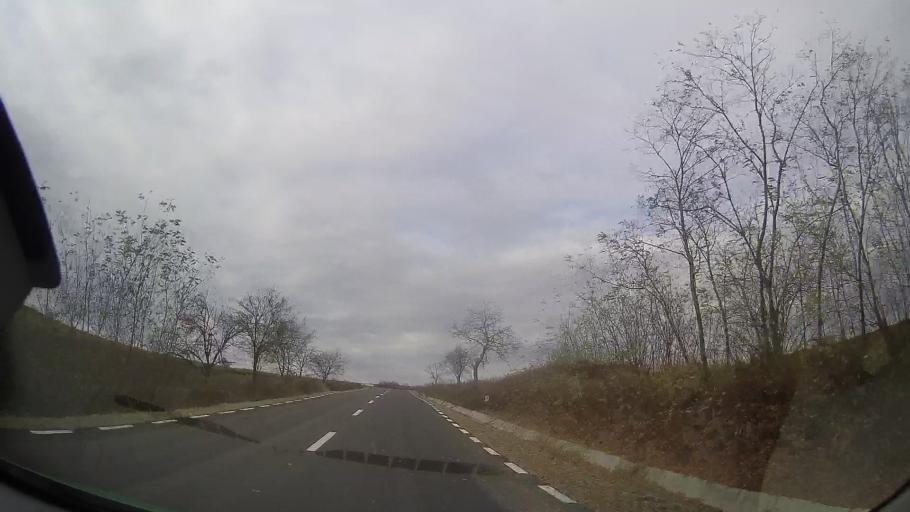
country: RO
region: Bistrita-Nasaud
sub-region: Comuna Teaca
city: Ocnita
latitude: 46.8270
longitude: 24.4759
